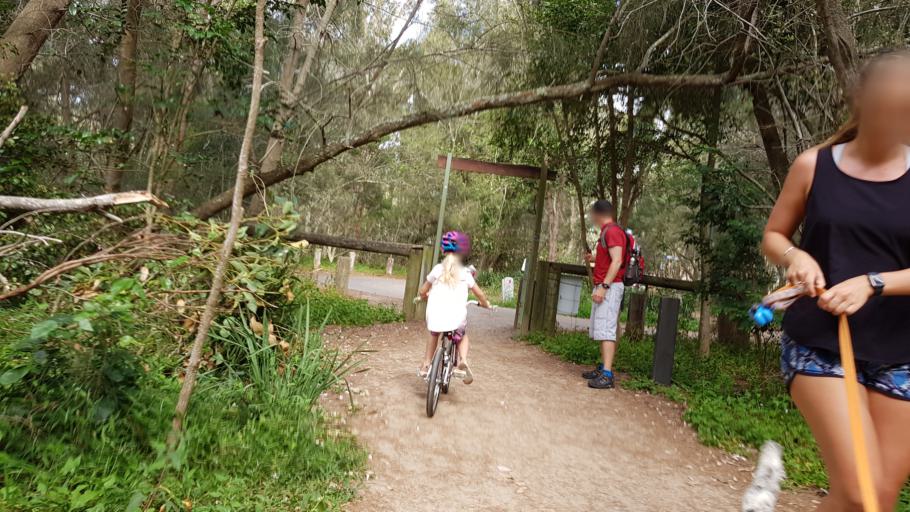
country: AU
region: New South Wales
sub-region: Pittwater
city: North Narrabeen
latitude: -33.7096
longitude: 151.2852
